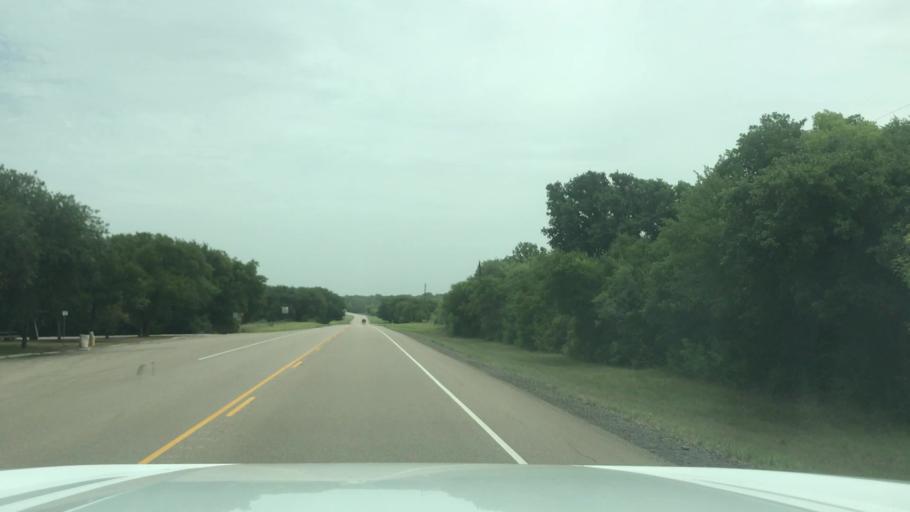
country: US
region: Texas
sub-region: Hamilton County
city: Hico
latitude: 31.9775
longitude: -97.8913
